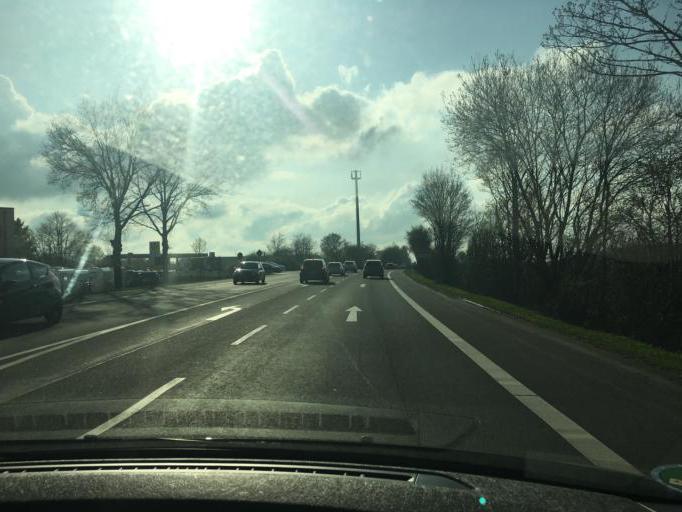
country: DE
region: North Rhine-Westphalia
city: Bornheim
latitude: 50.7240
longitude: 6.9236
